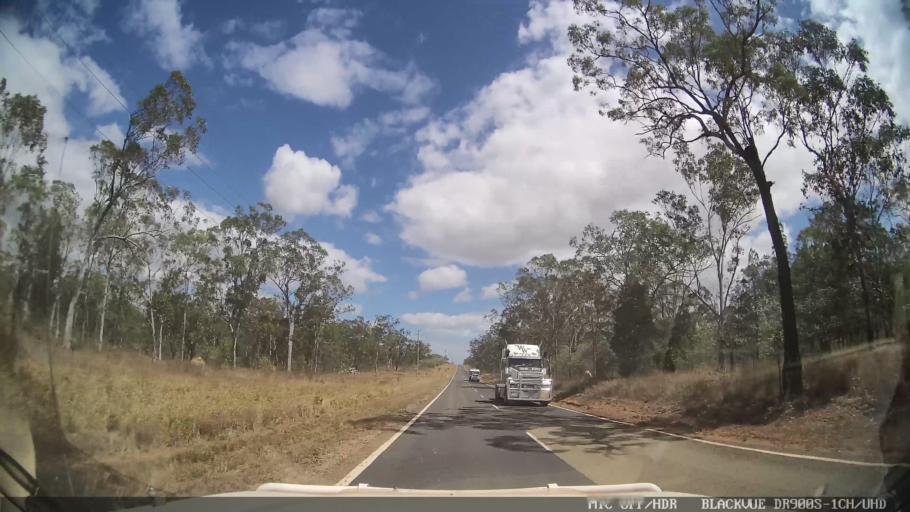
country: AU
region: Queensland
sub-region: Tablelands
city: Ravenshoe
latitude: -17.7264
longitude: 145.0483
